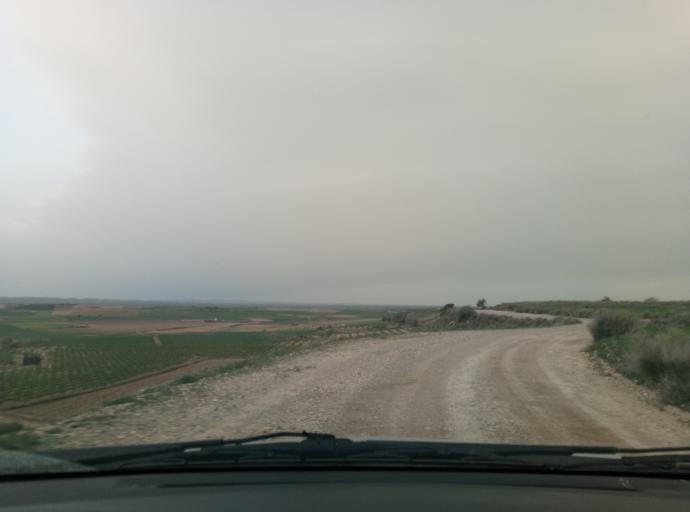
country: ES
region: Catalonia
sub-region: Provincia de Lleida
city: Verdu
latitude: 41.6127
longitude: 1.1085
